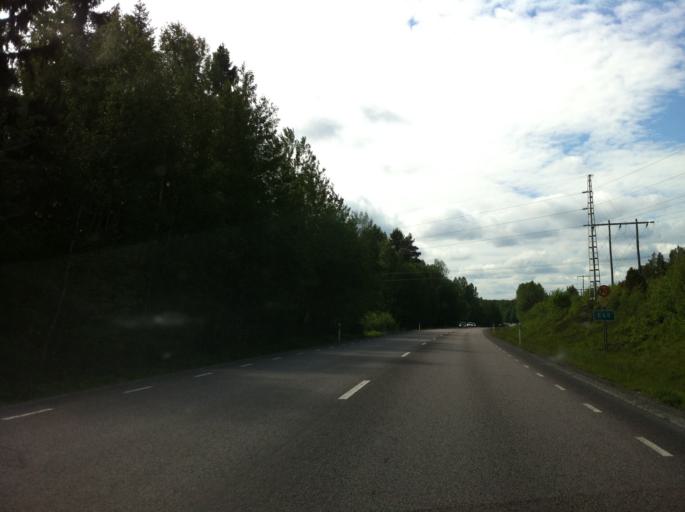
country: SE
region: Vaermland
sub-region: Karlstads Kommun
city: Valberg
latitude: 59.3940
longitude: 13.1794
